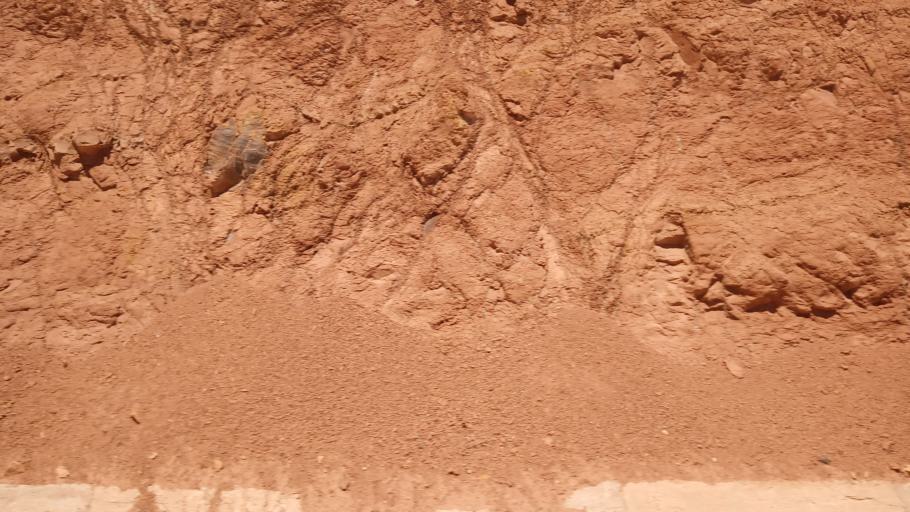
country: TR
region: Malatya
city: Darende
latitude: 38.6250
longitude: 37.4545
